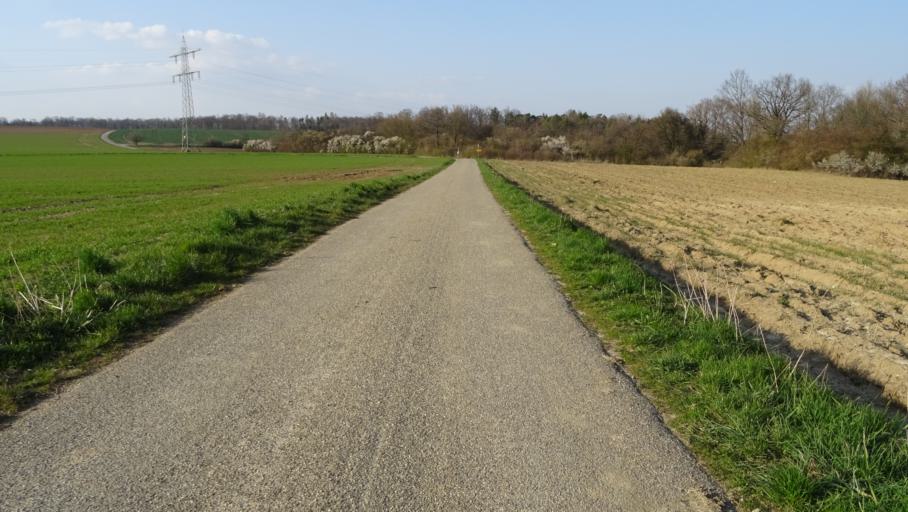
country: DE
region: Baden-Wuerttemberg
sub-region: Regierungsbezirk Stuttgart
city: Roigheim
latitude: 49.3811
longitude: 9.3577
